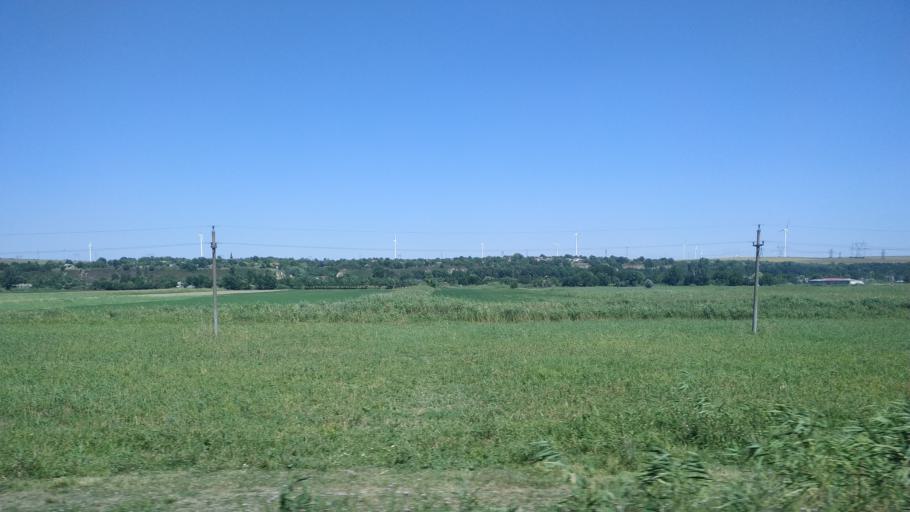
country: RO
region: Constanta
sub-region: Comuna Saligny
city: Faclia
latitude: 44.2721
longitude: 28.1069
